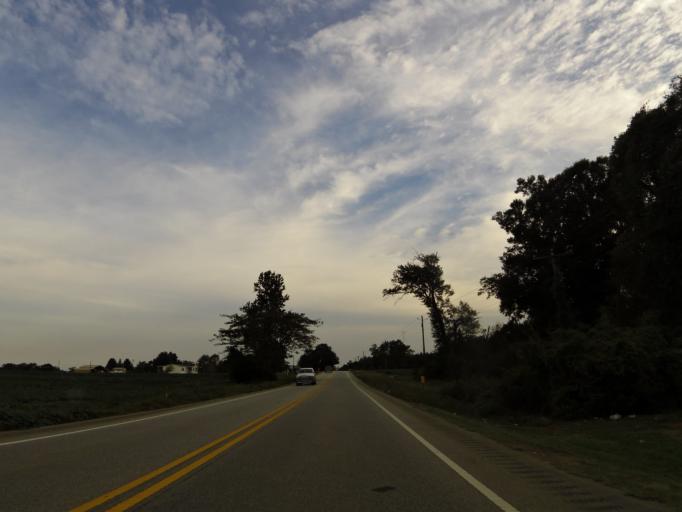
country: US
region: Alabama
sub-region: Monroe County
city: Frisco City
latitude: 31.2773
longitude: -87.5024
